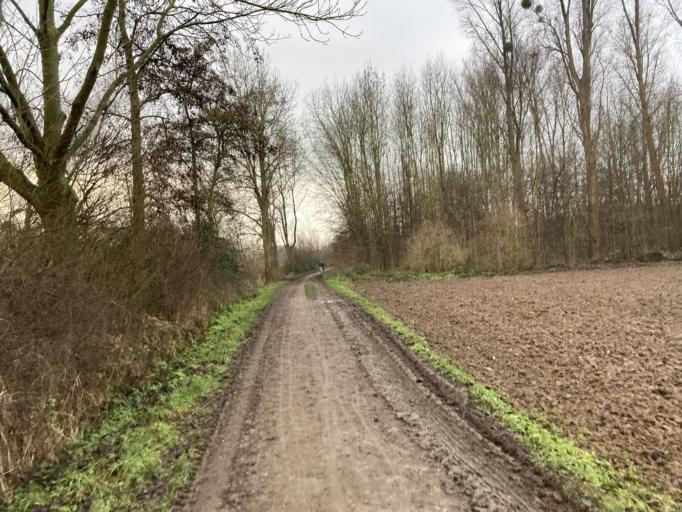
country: DE
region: North Rhine-Westphalia
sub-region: Regierungsbezirk Dusseldorf
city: Neubrueck
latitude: 51.1210
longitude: 6.6341
